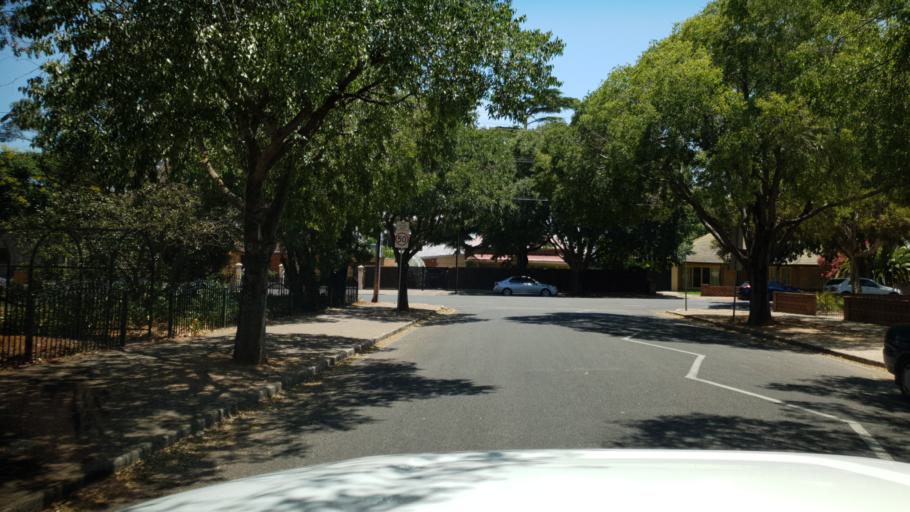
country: AU
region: South Australia
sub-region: Mitcham
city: Clarence Gardens
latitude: -34.9784
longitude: 138.5792
